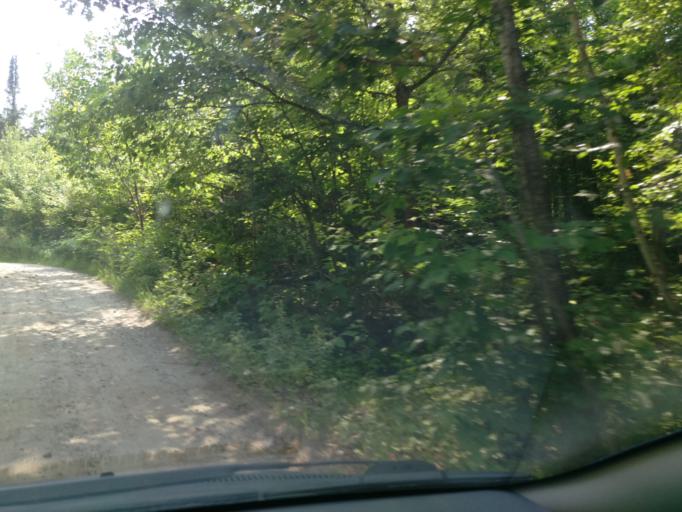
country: CA
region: Quebec
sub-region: Outaouais
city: Maniwaki
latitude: 46.2036
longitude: -76.1418
